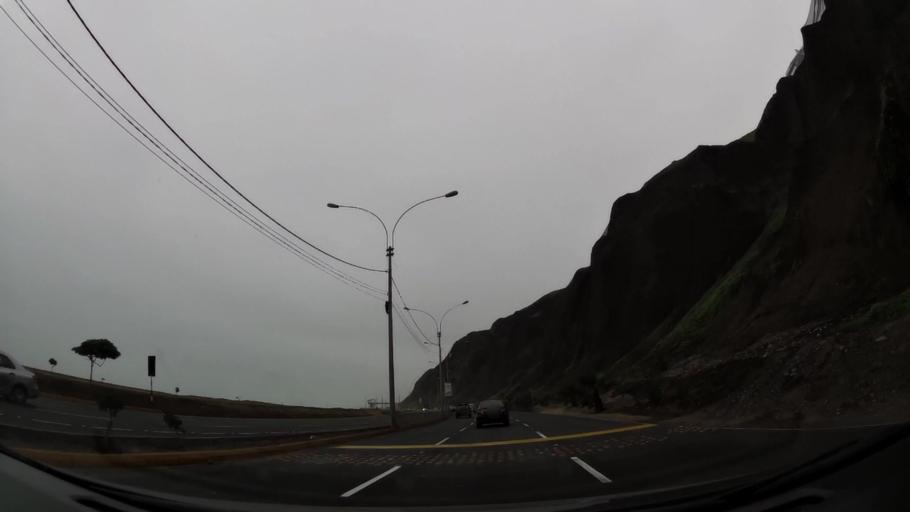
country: PE
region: Lima
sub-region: Lima
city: San Isidro
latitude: -12.1195
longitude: -77.0457
